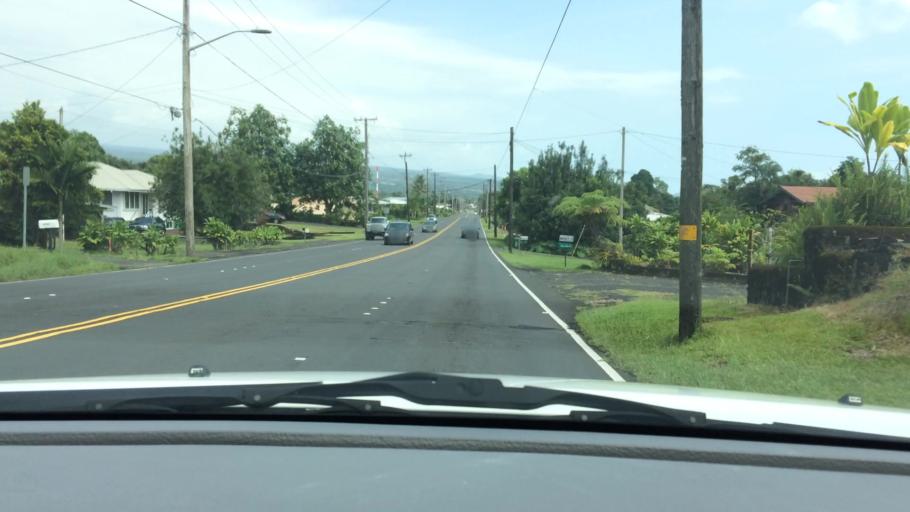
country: US
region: Hawaii
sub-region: Hawaii County
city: Hilo
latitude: 19.6975
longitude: -155.0691
